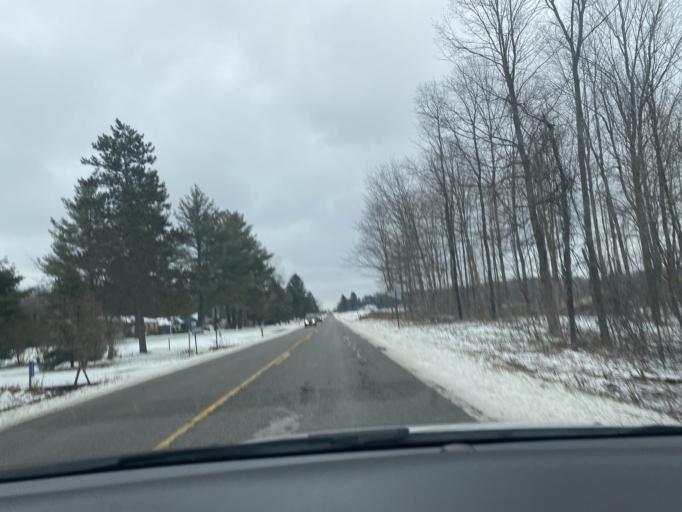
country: US
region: Michigan
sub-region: Lapeer County
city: Barnes Lake-Millers Lake
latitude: 43.2052
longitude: -83.2899
